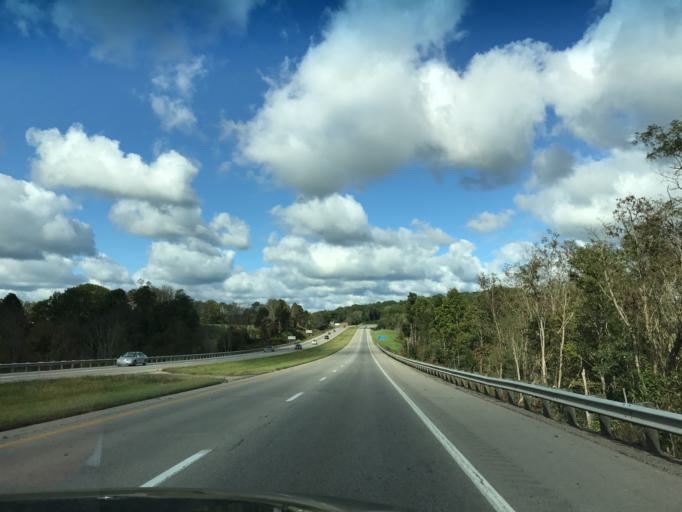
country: US
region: Ohio
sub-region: Hocking County
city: Logan
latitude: 39.5489
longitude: -82.4661
